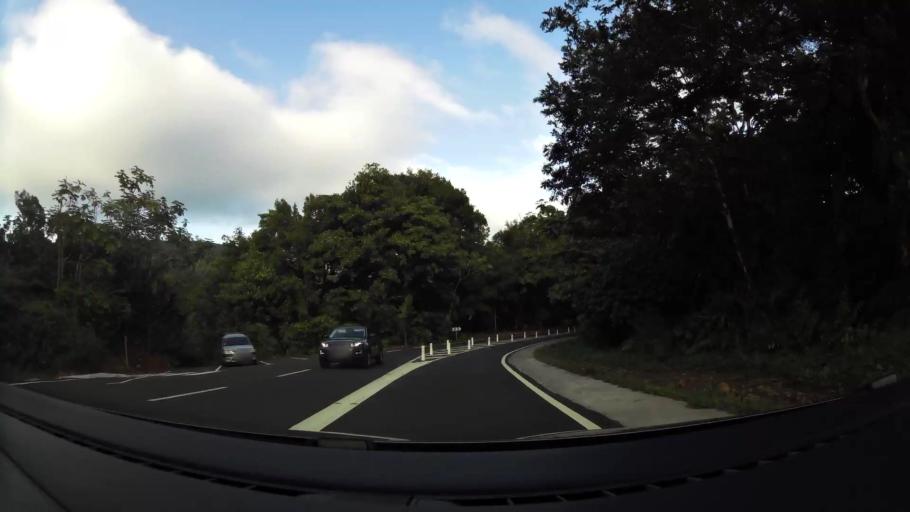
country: GP
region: Guadeloupe
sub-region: Guadeloupe
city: Bouillante
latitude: 16.1800
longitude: -61.7164
